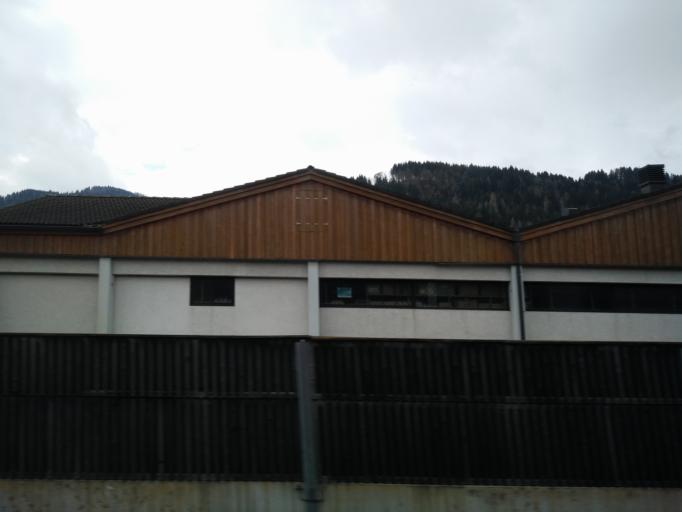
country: AT
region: Salzburg
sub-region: Politischer Bezirk Sankt Johann im Pongau
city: Bischofshofen
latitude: 47.4067
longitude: 13.2185
